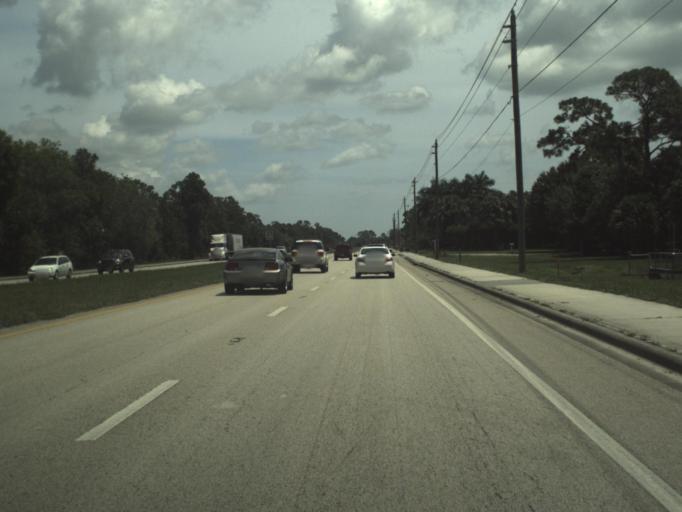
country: US
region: Florida
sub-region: Martin County
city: Palm City
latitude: 27.1376
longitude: -80.2487
